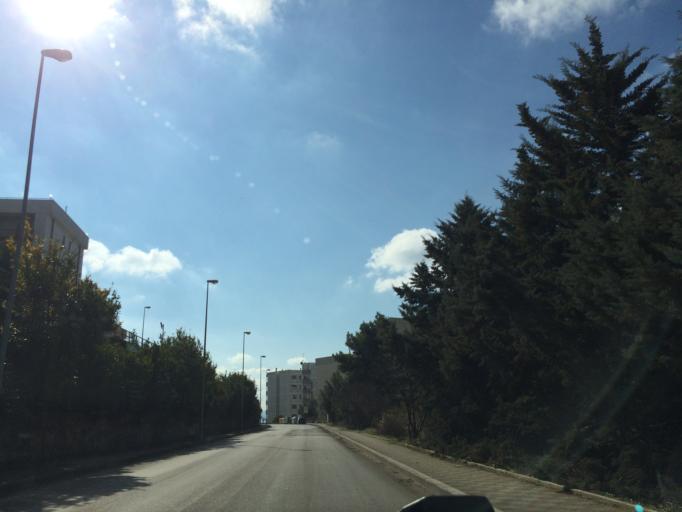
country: IT
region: Basilicate
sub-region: Provincia di Matera
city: Matera
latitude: 40.6717
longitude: 16.5886
